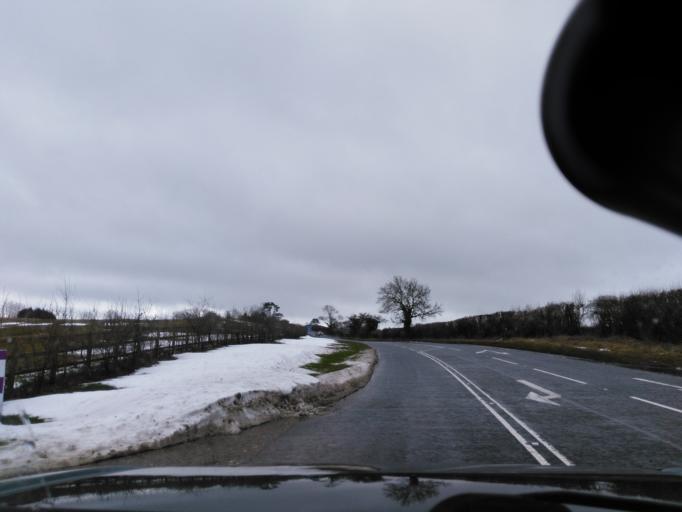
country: GB
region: England
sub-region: Wiltshire
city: Bradford-on-Avon
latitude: 51.3638
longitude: -2.2644
